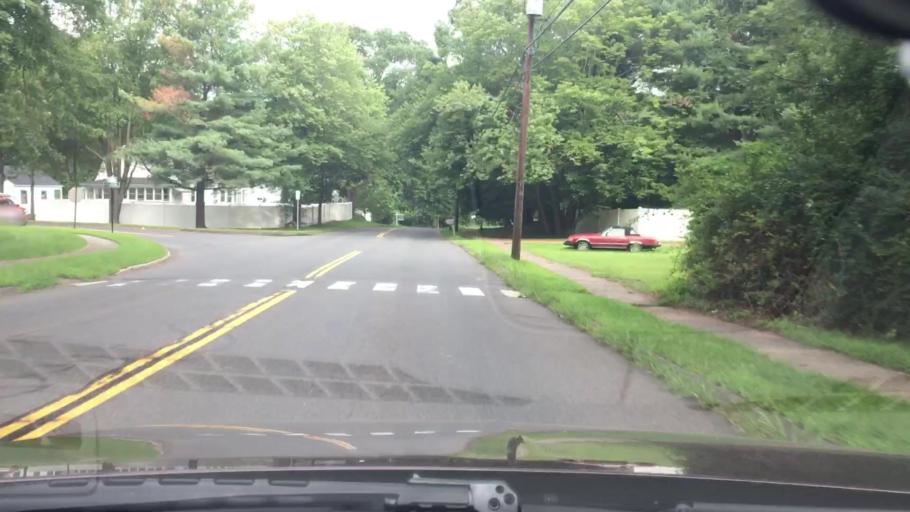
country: US
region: Connecticut
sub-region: Tolland County
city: Rockville
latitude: 41.8305
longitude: -72.4914
